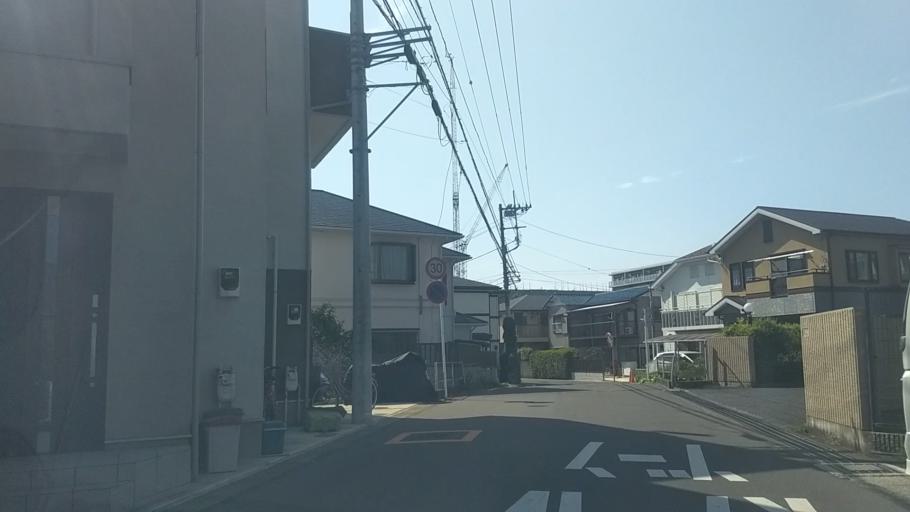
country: JP
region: Kanagawa
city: Kamakura
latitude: 35.3547
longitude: 139.5405
